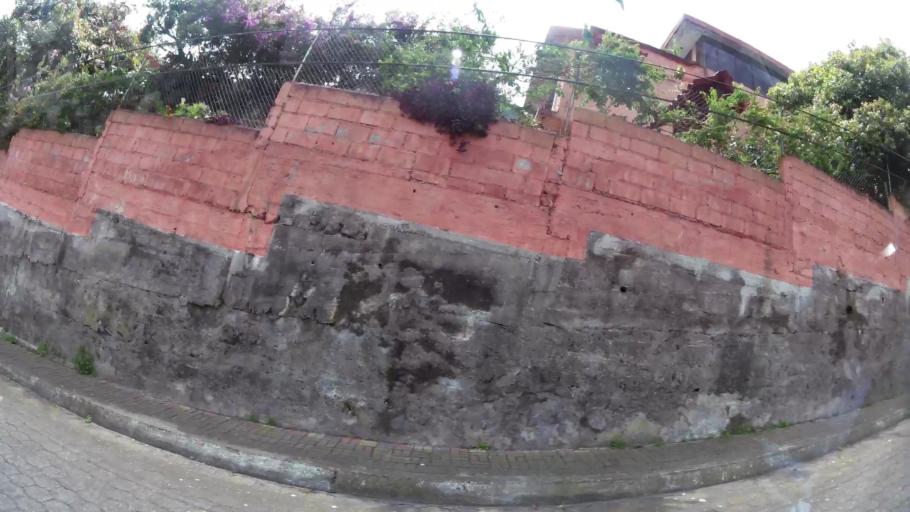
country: EC
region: Tungurahua
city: Banos
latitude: -1.3987
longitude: -78.4268
